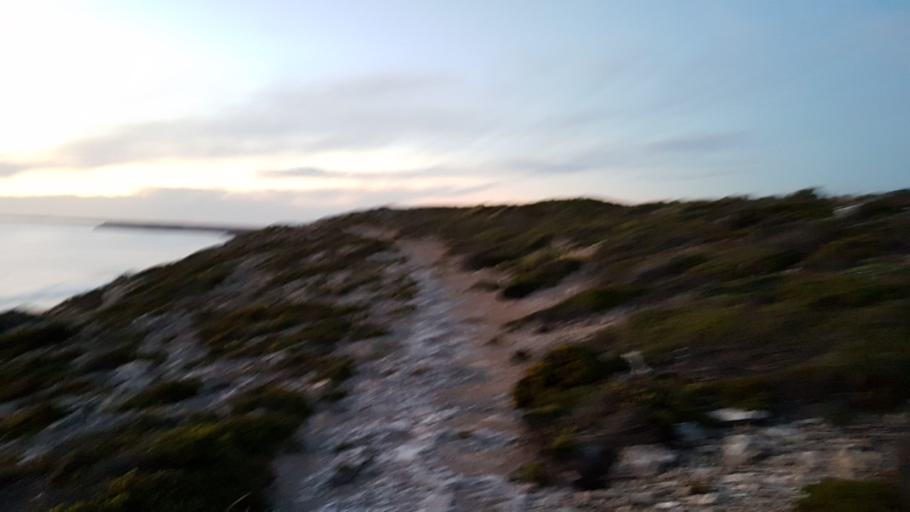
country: AU
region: South Australia
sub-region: Yorke Peninsula
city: Honiton
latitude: -35.2368
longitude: 137.1054
